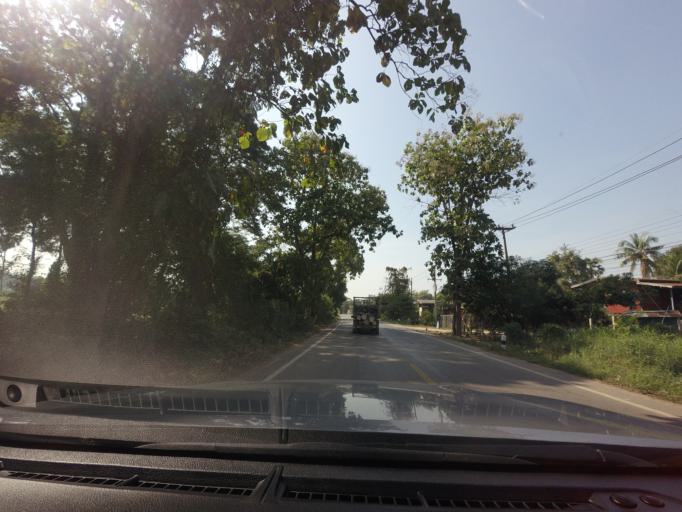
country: TH
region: Sukhothai
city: Kong Krailat
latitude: 16.8543
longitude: 99.9442
